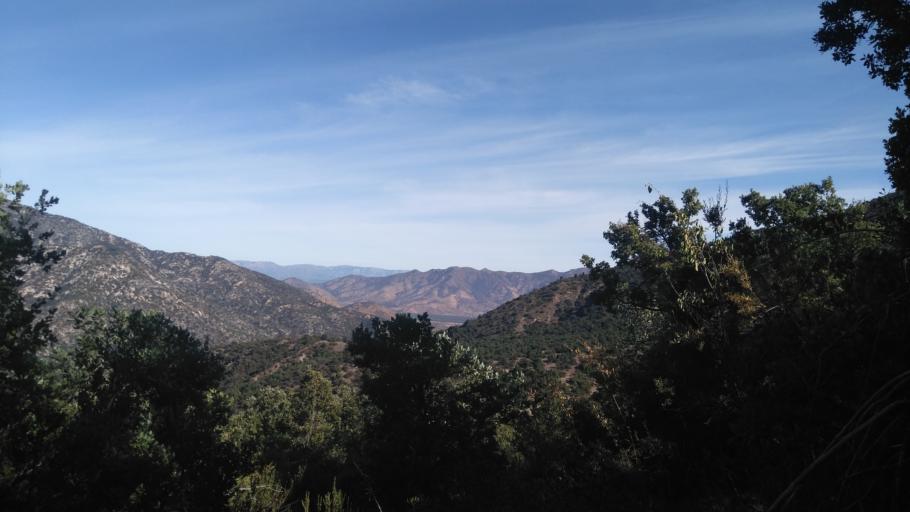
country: CL
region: Santiago Metropolitan
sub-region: Provincia de Cordillera
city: Puente Alto
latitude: -33.7131
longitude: -70.4582
